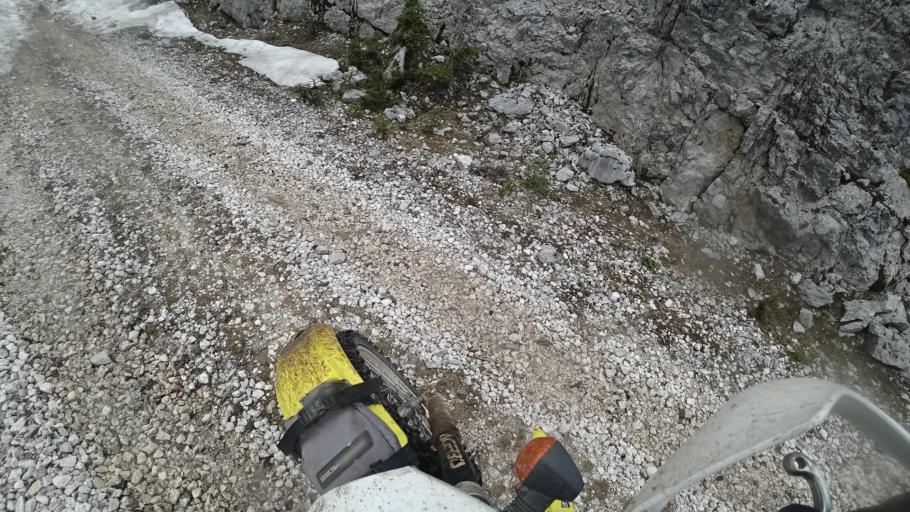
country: BA
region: Republika Srpska
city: Sipovo
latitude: 44.1266
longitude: 17.0484
